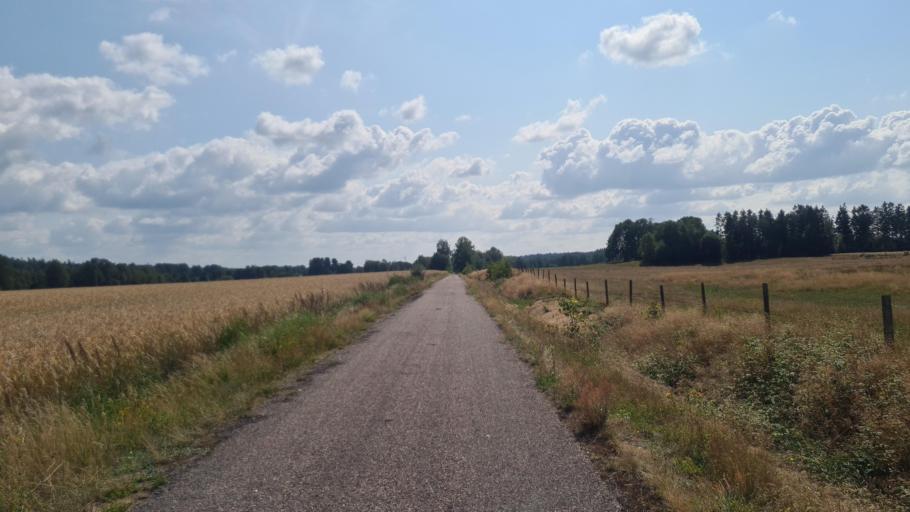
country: SE
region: Kronoberg
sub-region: Ljungby Kommun
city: Ljungby
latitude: 56.8002
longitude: 13.9131
